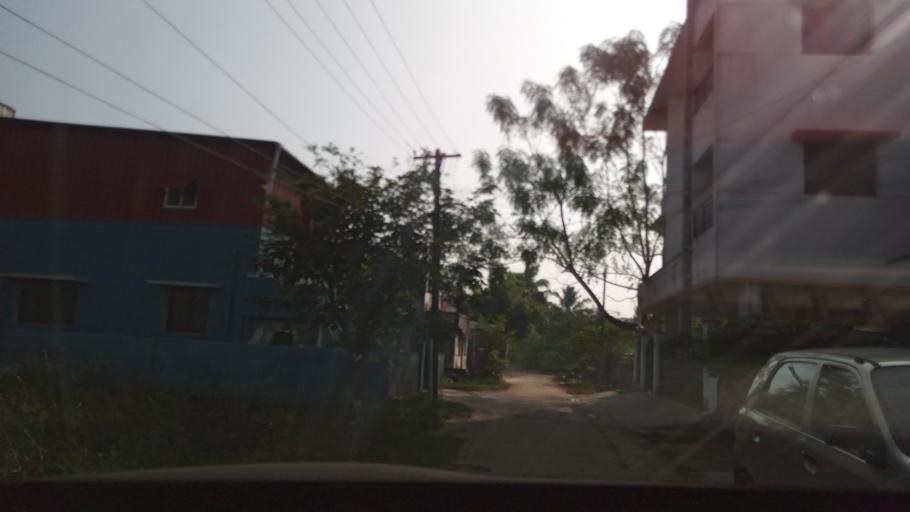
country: IN
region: Tamil Nadu
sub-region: Kancheepuram
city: Guduvancheri
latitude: 12.8522
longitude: 80.0693
